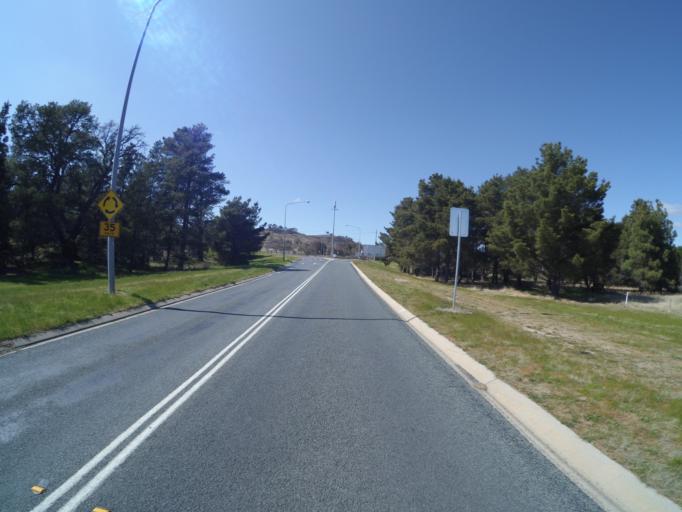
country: AU
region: Australian Capital Territory
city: Macarthur
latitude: -35.4355
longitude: 149.1233
